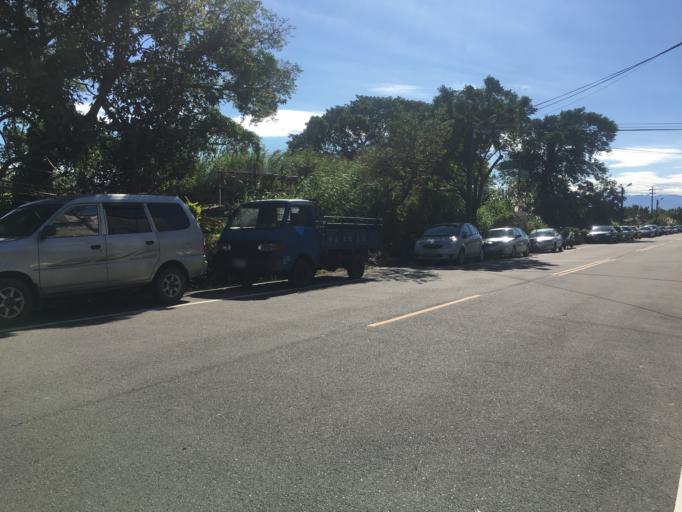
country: TW
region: Taiwan
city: Daxi
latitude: 24.9029
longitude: 121.2170
